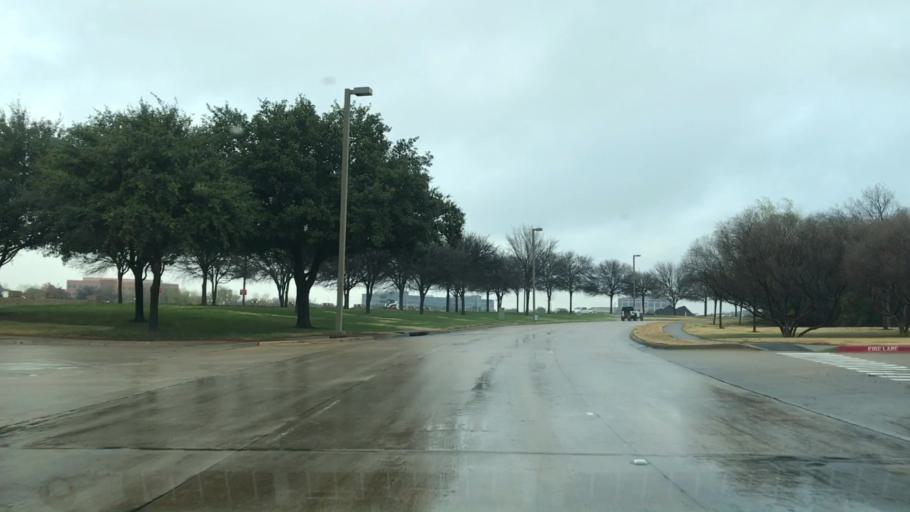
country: US
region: Texas
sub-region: Dallas County
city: Farmers Branch
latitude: 32.9000
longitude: -96.9536
